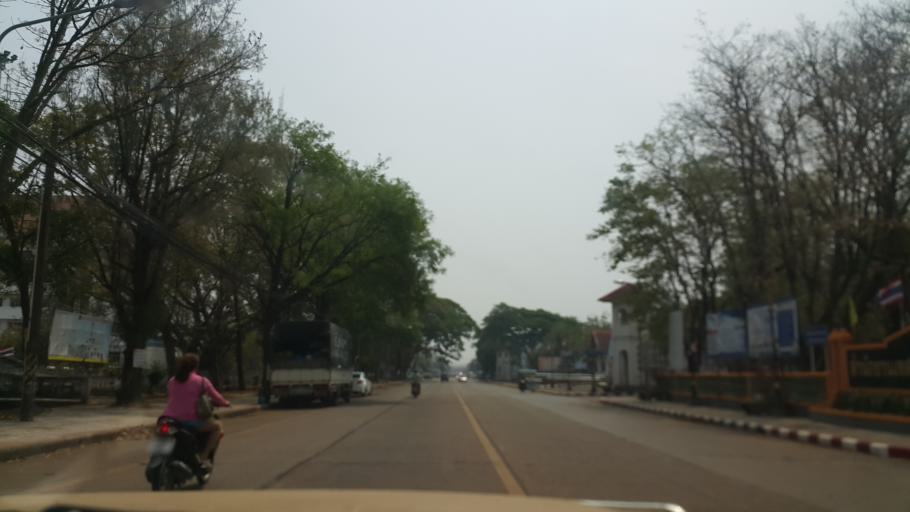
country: TH
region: Nakhon Phanom
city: Nakhon Phanom
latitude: 17.4079
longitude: 104.7810
